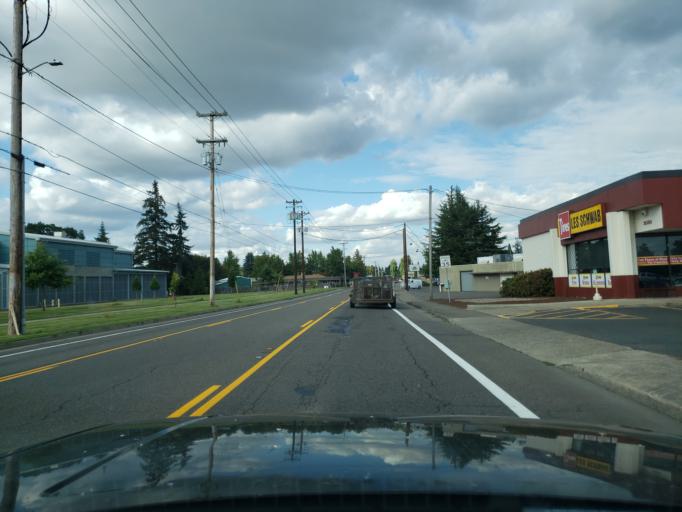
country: US
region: Oregon
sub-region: Marion County
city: Keizer
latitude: 44.9698
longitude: -123.0316
